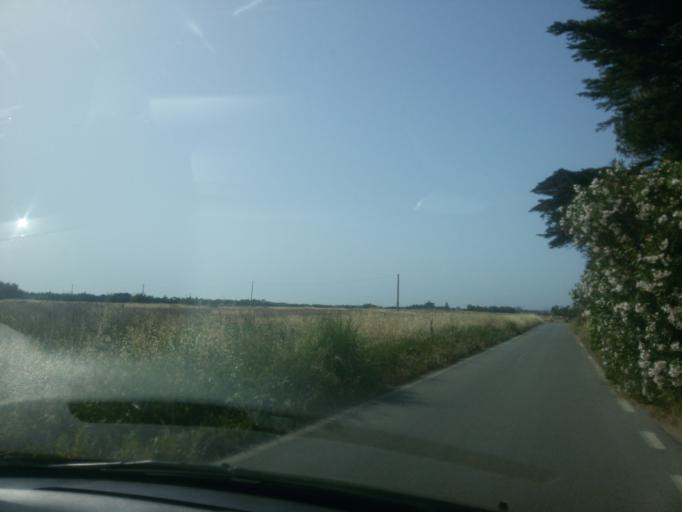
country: IT
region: Apulia
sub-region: Provincia di Brindisi
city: Brindisi
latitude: 40.6791
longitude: 17.8867
